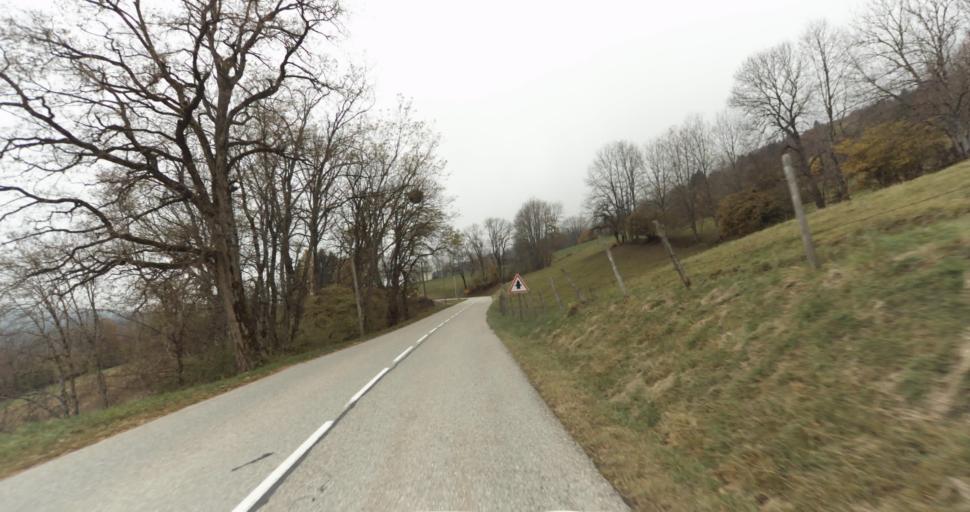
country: FR
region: Rhone-Alpes
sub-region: Departement de la Haute-Savoie
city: Saint-Jorioz
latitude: 45.7924
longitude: 6.1361
